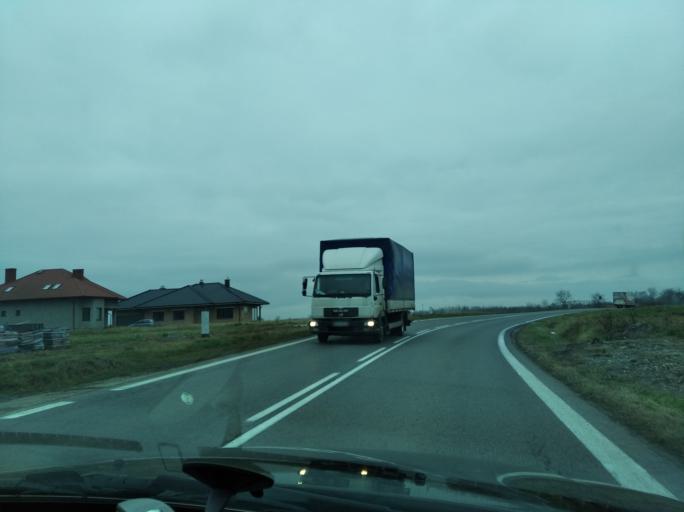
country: PL
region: Subcarpathian Voivodeship
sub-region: Powiat lancucki
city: Zolynia
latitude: 50.1754
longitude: 22.3139
